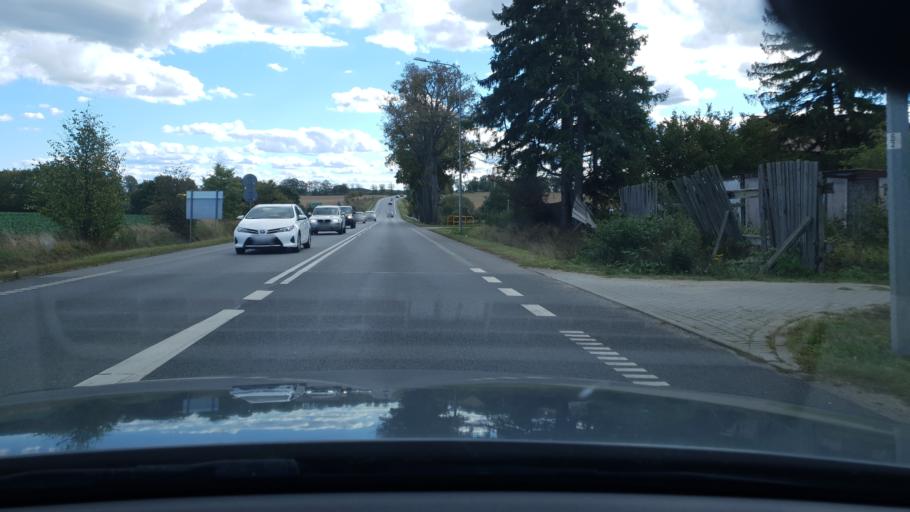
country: PL
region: Pomeranian Voivodeship
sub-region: Powiat pucki
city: Zelistrzewo
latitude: 54.6794
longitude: 18.3734
